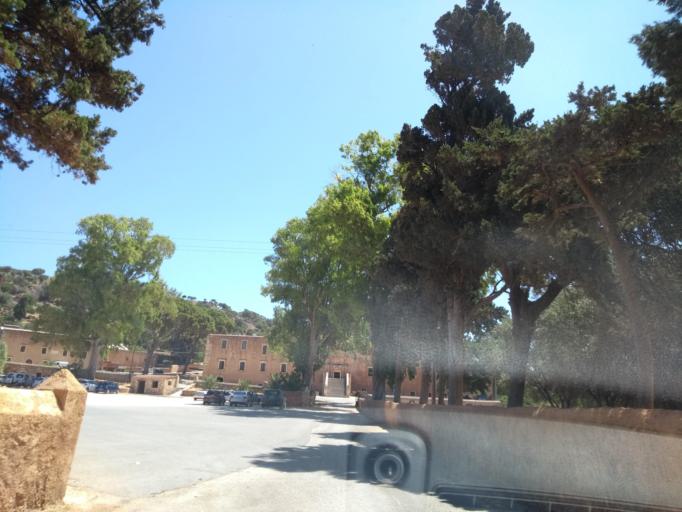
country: GR
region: Crete
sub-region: Nomos Chanias
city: Mouzouras
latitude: 35.5603
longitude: 24.1337
